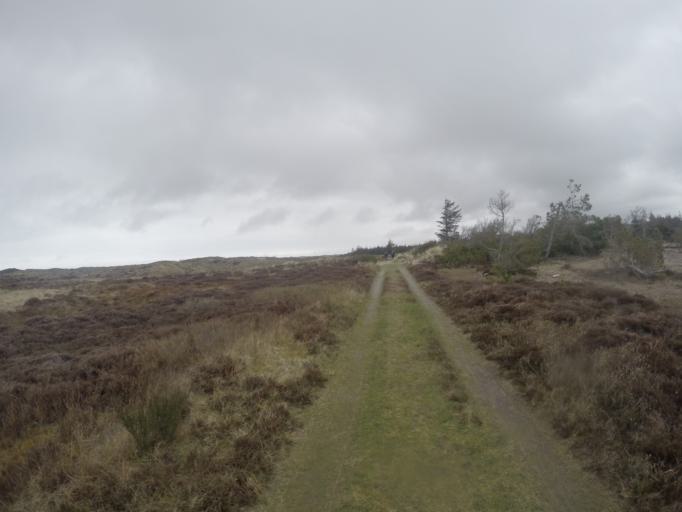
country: DK
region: North Denmark
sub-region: Thisted Kommune
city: Hurup
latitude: 56.9080
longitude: 8.3471
